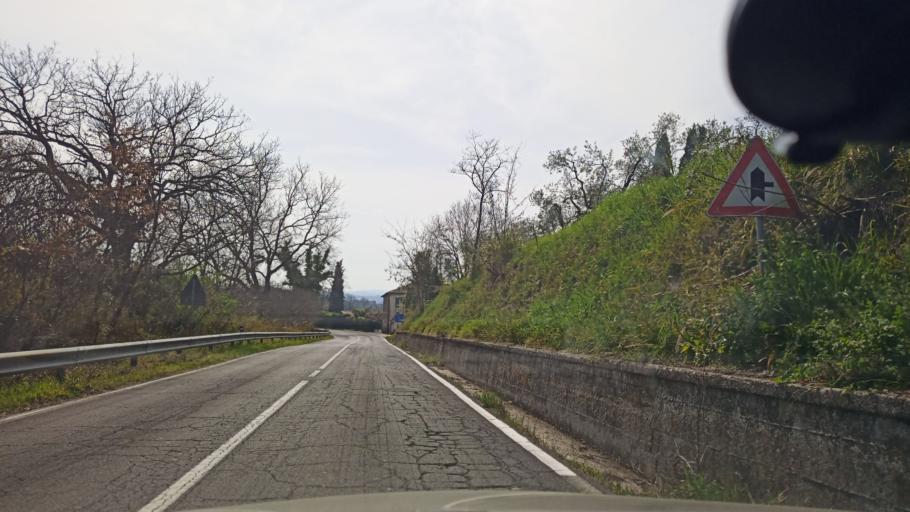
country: IT
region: Latium
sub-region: Provincia di Rieti
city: Torri in Sabina
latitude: 42.3497
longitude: 12.6499
